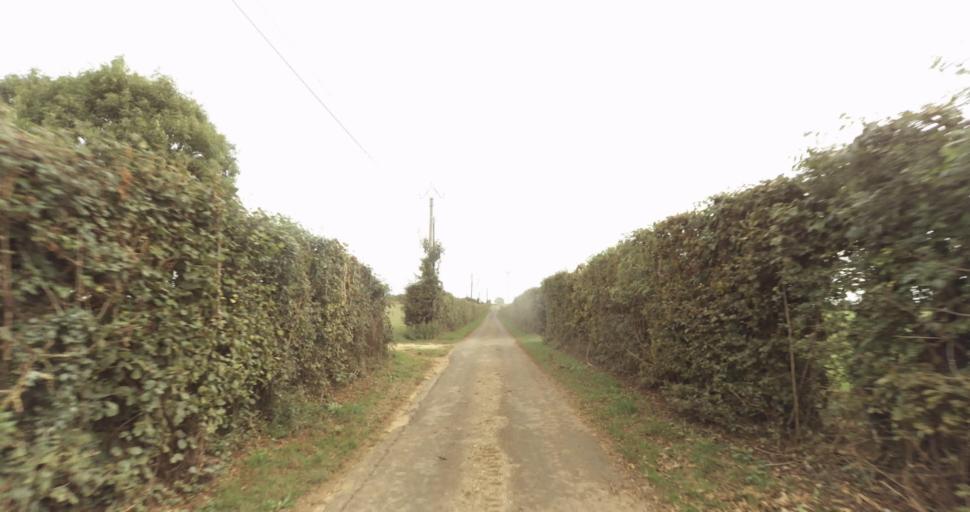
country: FR
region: Lower Normandy
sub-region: Departement de l'Orne
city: Sainte-Gauburge-Sainte-Colombe
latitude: 48.7288
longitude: 0.3652
